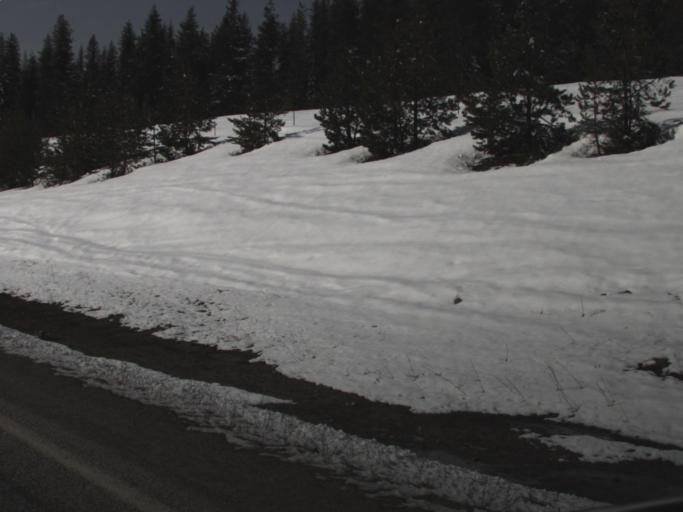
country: US
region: Washington
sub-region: Stevens County
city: Colville
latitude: 48.6634
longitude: -117.4762
